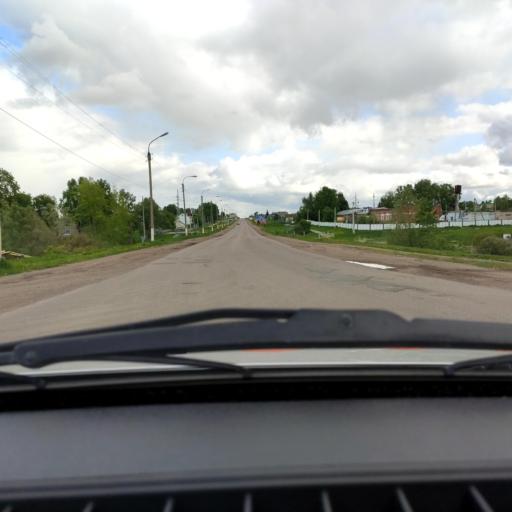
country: RU
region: Bashkortostan
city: Tolbazy
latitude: 54.0010
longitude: 55.8994
